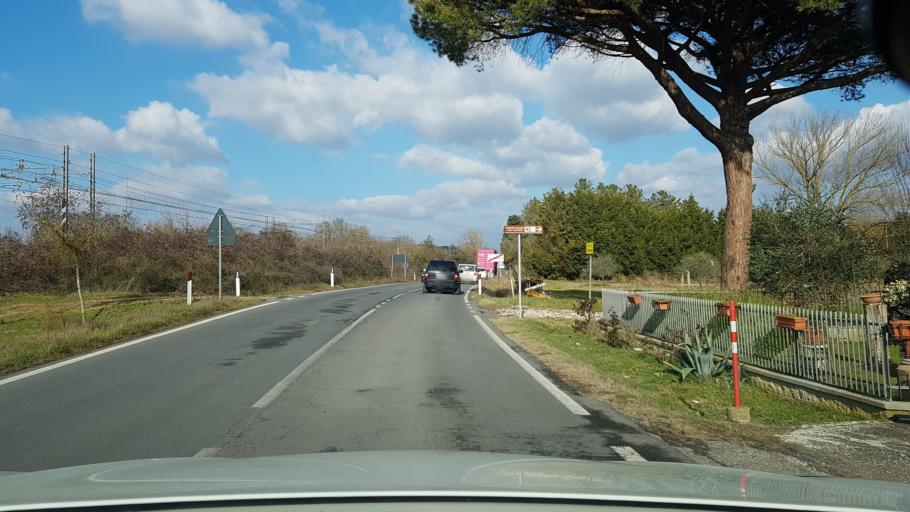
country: IT
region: Umbria
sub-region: Provincia di Perugia
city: Castiglione del Lago
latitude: 43.1546
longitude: 12.0189
